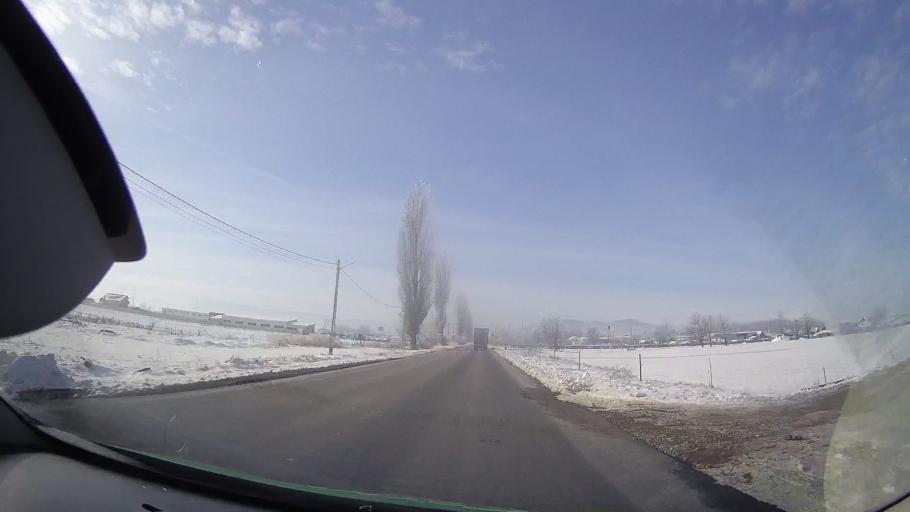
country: RO
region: Neamt
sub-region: Comuna Raucesti
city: Raucesti
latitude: 47.2093
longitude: 26.4084
